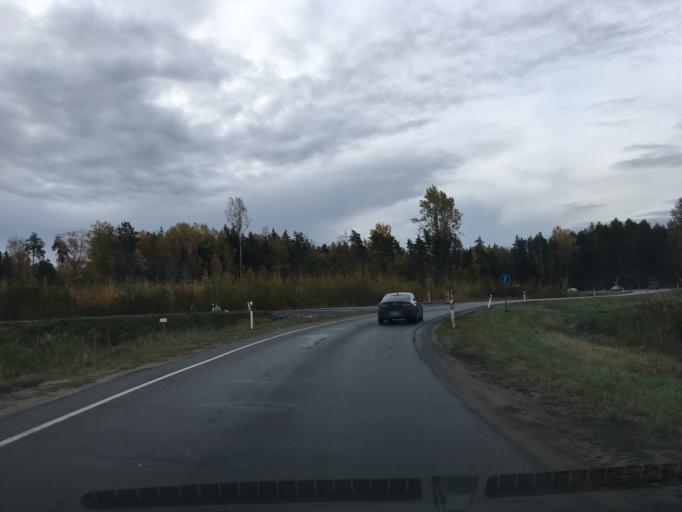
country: EE
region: Harju
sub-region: Saku vald
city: Saku
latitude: 59.3154
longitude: 24.6741
